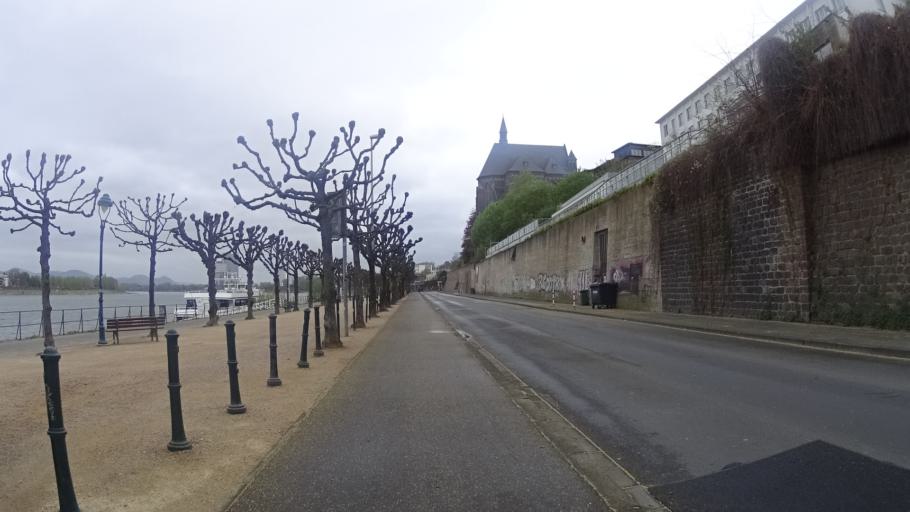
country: DE
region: North Rhine-Westphalia
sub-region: Regierungsbezirk Koln
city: Bonn
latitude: 50.7341
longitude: 7.1086
